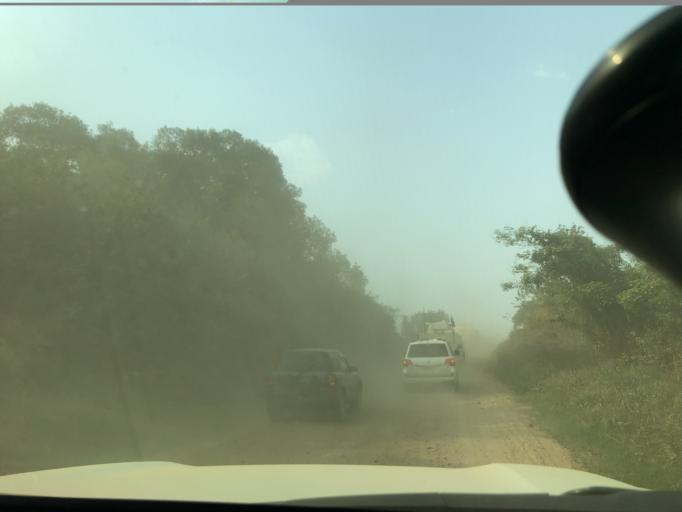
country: CD
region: Nord Kivu
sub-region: North Kivu
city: Butembo
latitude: 0.1334
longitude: 29.6423
